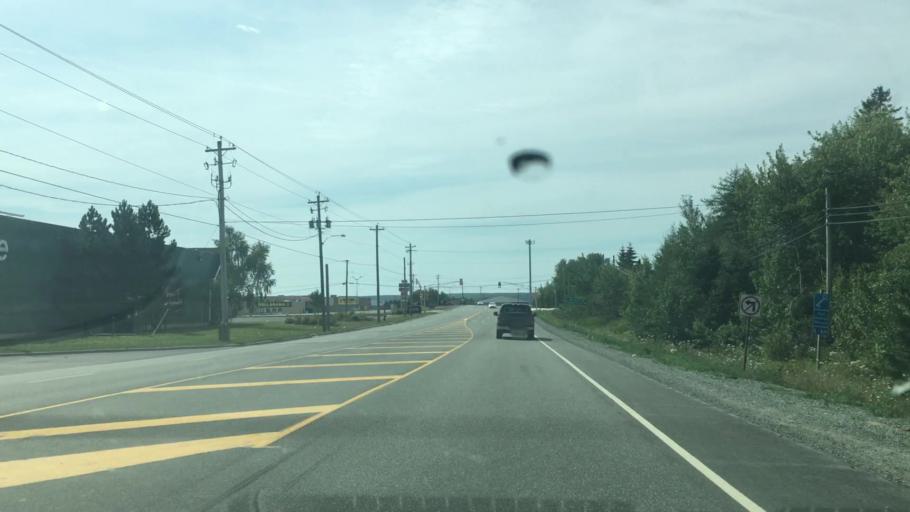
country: CA
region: Nova Scotia
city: Port Hawkesbury
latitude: 45.6199
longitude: -61.3344
